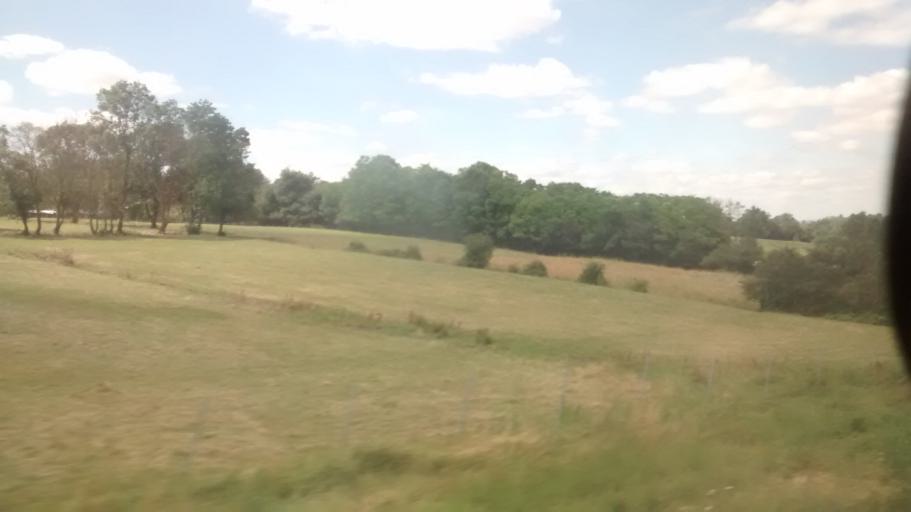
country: FR
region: Rhone-Alpes
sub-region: Departement de l'Ain
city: Saint-Didier-sur-Chalaronne
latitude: 46.1986
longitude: 4.8567
